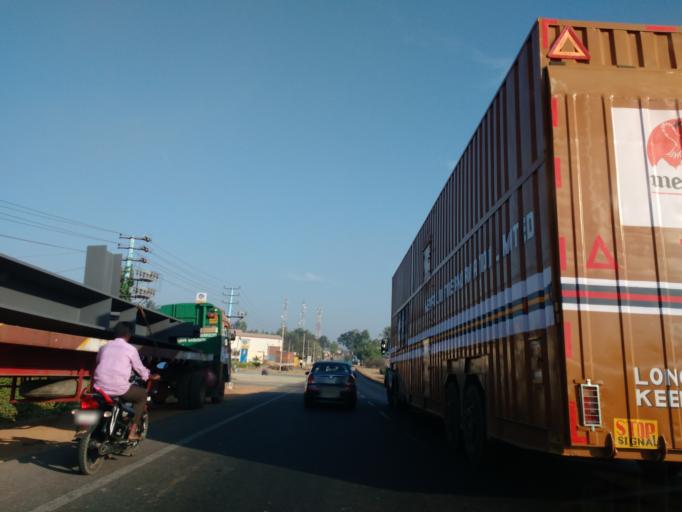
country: IN
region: Karnataka
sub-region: Bangalore Rural
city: Nelamangala
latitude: 13.1448
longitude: 77.3435
